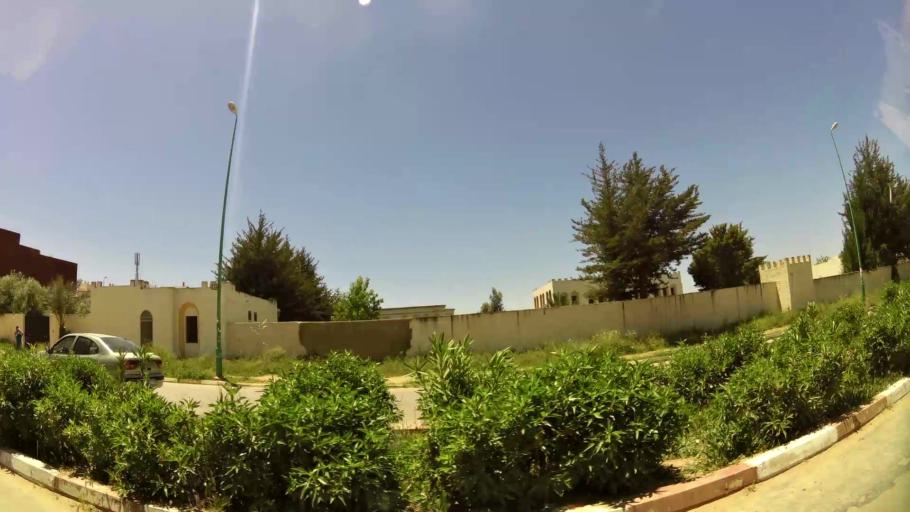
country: MA
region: Meknes-Tafilalet
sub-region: Meknes
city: Meknes
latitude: 33.8578
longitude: -5.5698
